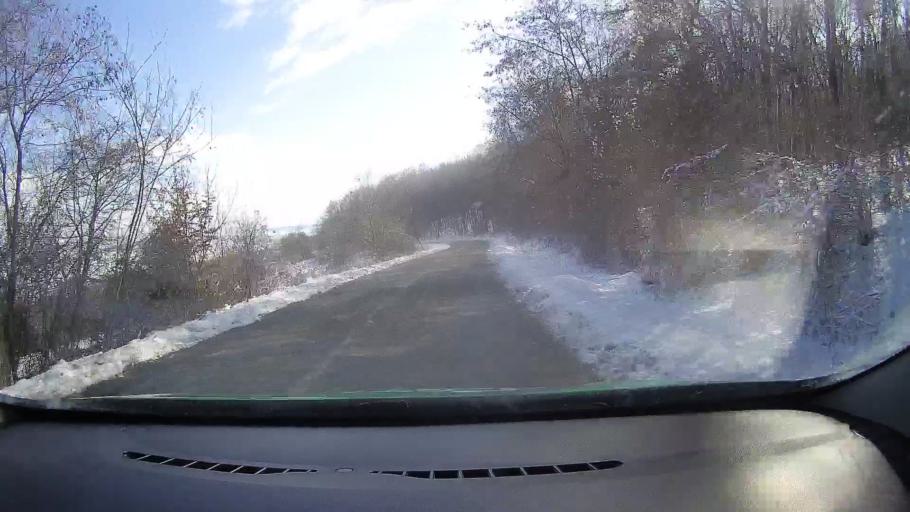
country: RO
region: Sibiu
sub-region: Comuna Altina
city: Altina
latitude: 45.9928
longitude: 24.4311
